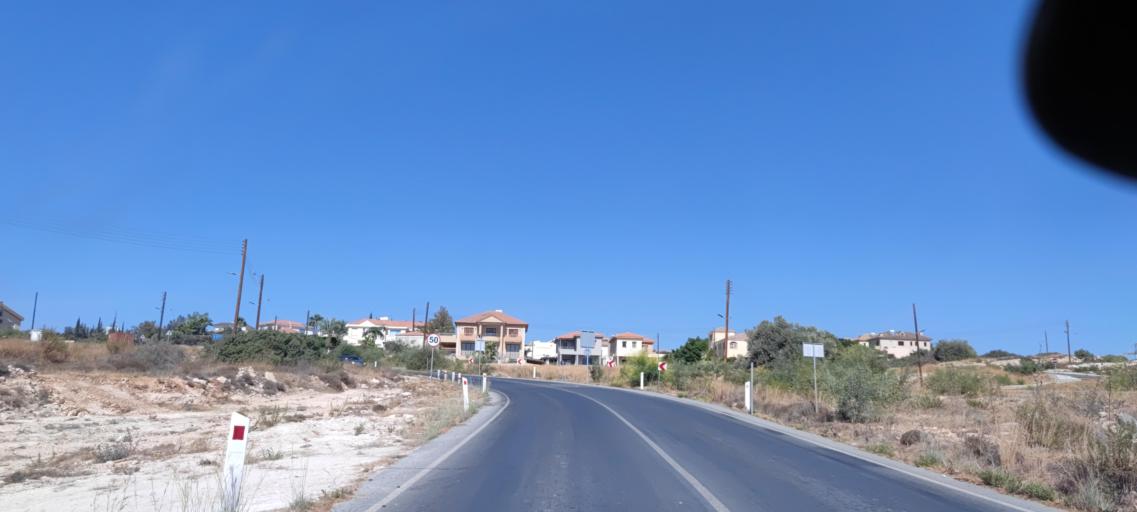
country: CY
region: Limassol
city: Mouttagiaka
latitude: 34.7218
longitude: 33.0659
